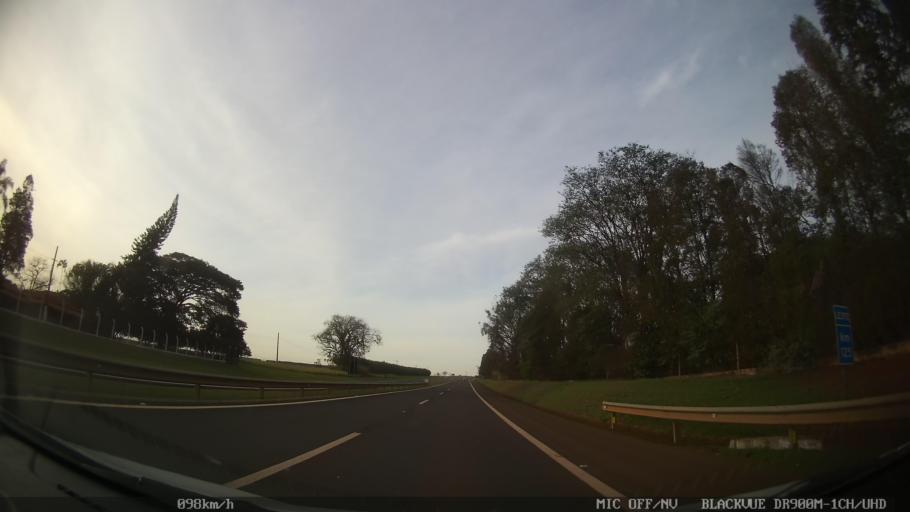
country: BR
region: Sao Paulo
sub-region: Iracemapolis
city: Iracemapolis
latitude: -22.6369
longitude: -47.5081
